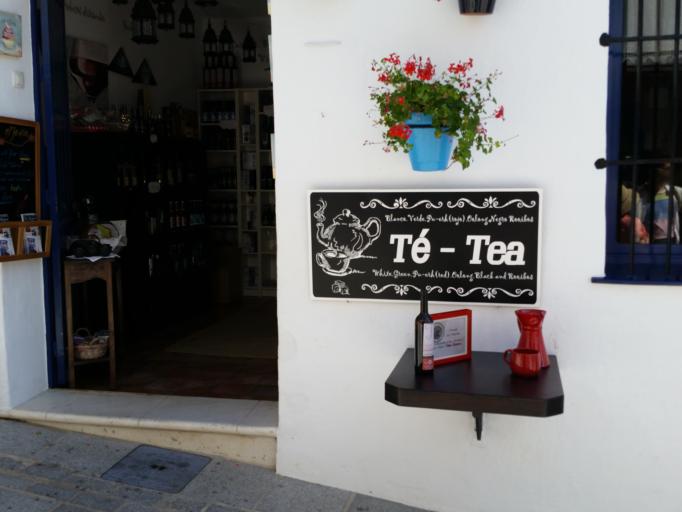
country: ES
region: Andalusia
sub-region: Provincia de Malaga
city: Mijas
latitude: 36.5953
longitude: -4.6392
